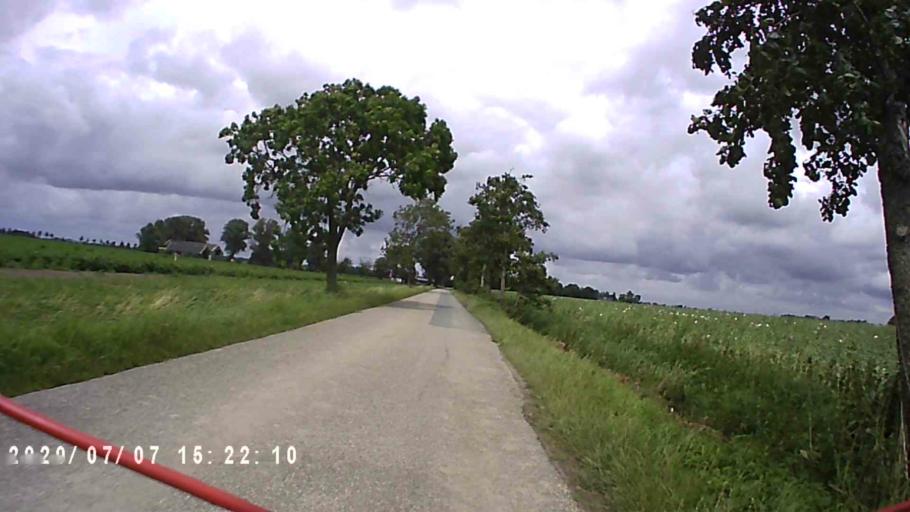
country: NL
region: Groningen
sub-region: Gemeente Winsum
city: Winsum
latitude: 53.3426
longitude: 6.4571
